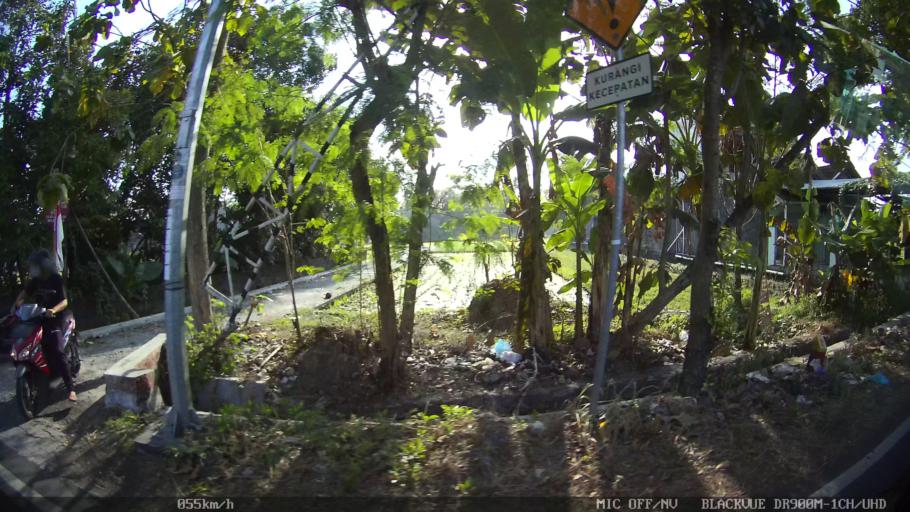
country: ID
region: Daerah Istimewa Yogyakarta
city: Bantul
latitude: -7.8803
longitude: 110.3194
